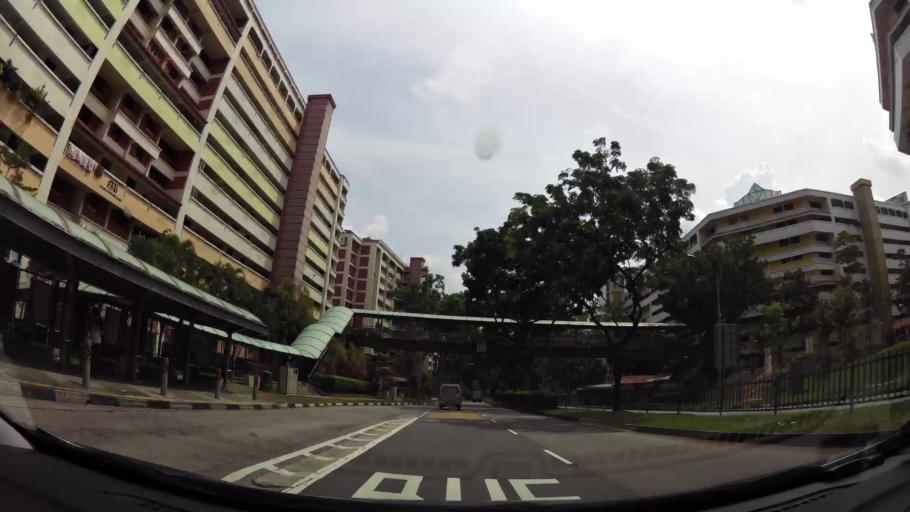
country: SG
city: Singapore
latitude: 1.3489
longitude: 103.7543
